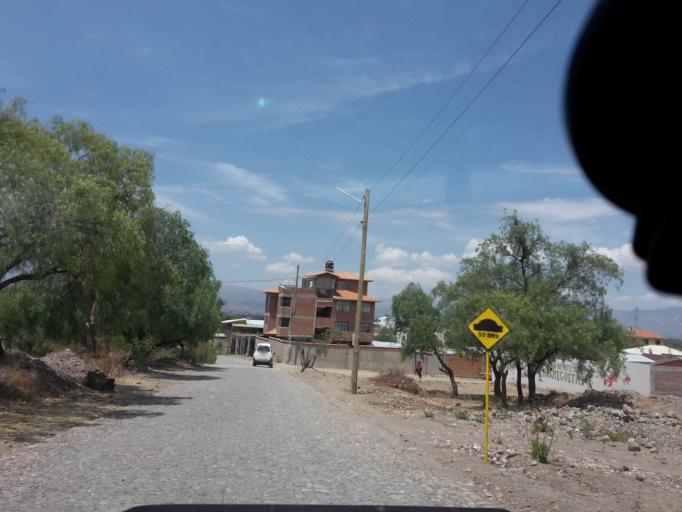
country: BO
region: Cochabamba
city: Cochabamba
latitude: -17.3258
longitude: -66.2230
